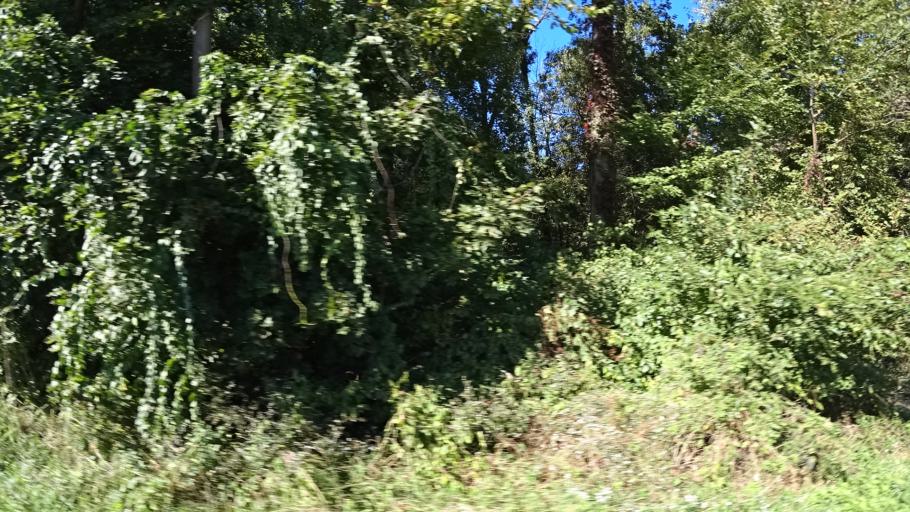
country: US
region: Indiana
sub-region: LaPorte County
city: Michigan City
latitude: 41.6836
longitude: -86.9133
